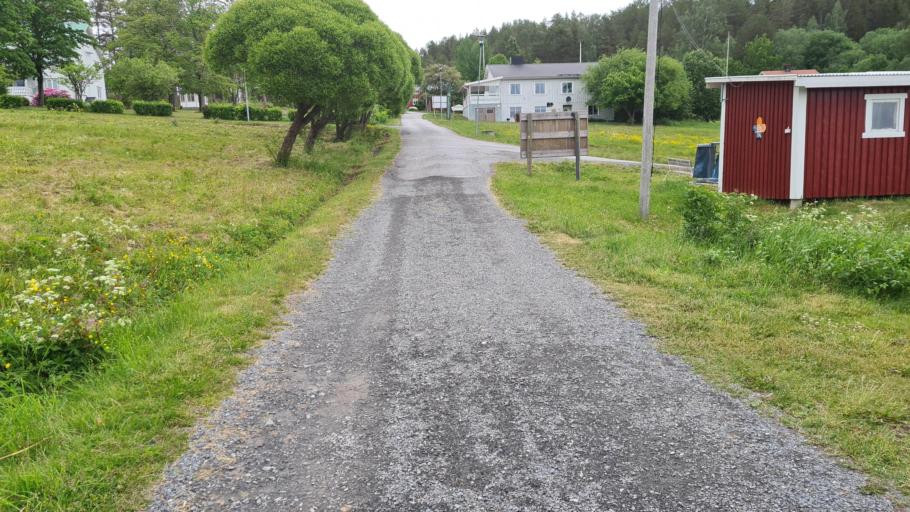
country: SE
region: Vaesternorrland
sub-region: Kramfors Kommun
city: Nordingra
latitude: 62.9715
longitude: 18.4244
